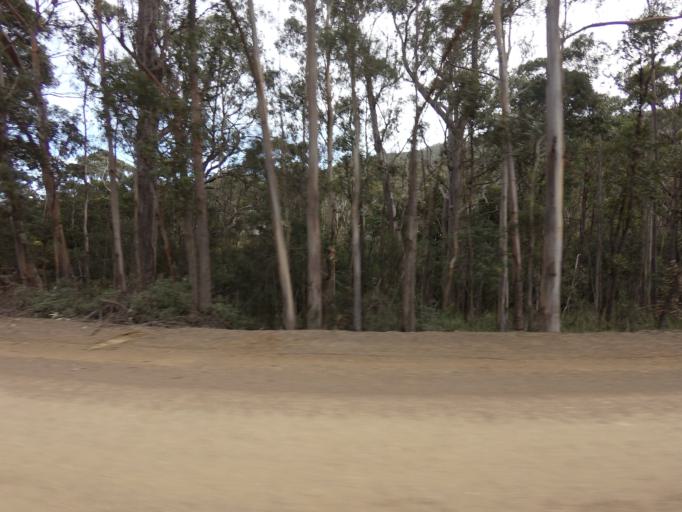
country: AU
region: Tasmania
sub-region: Huon Valley
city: Huonville
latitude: -43.0608
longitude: 147.0946
